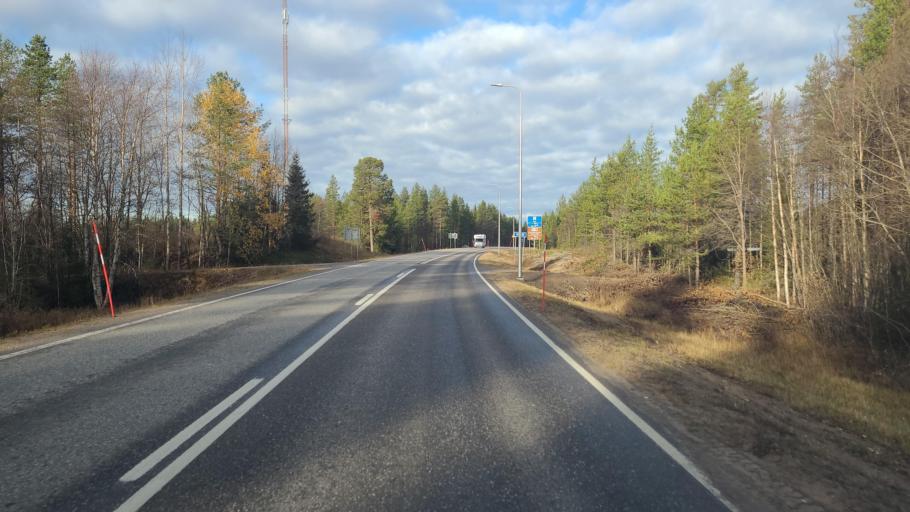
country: FI
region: Lapland
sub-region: Itae-Lappi
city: Posio
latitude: 66.1044
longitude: 28.1852
